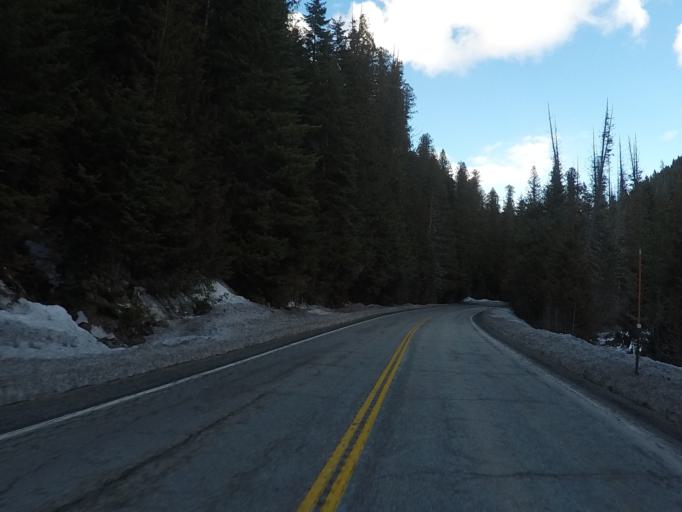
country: US
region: Montana
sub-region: Ravalli County
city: Stevensville
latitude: 46.5372
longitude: -114.6766
